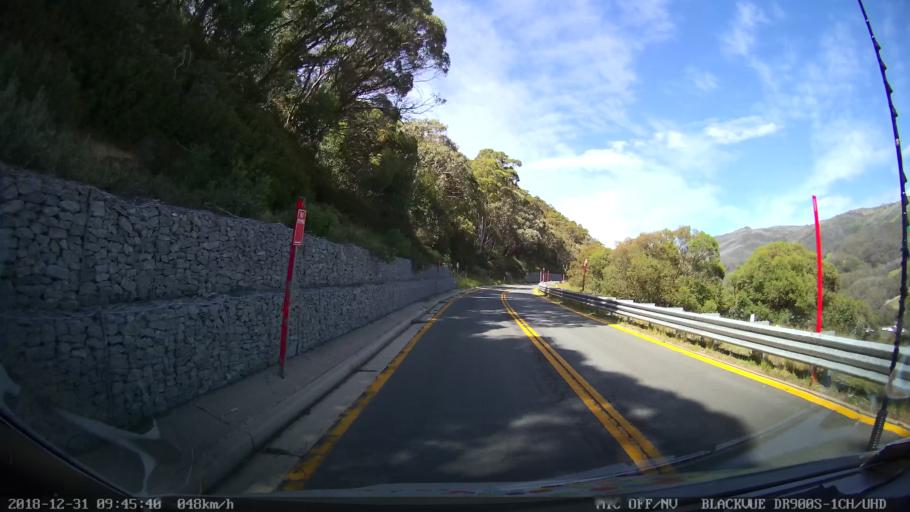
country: AU
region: New South Wales
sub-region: Snowy River
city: Jindabyne
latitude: -36.5006
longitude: 148.3160
